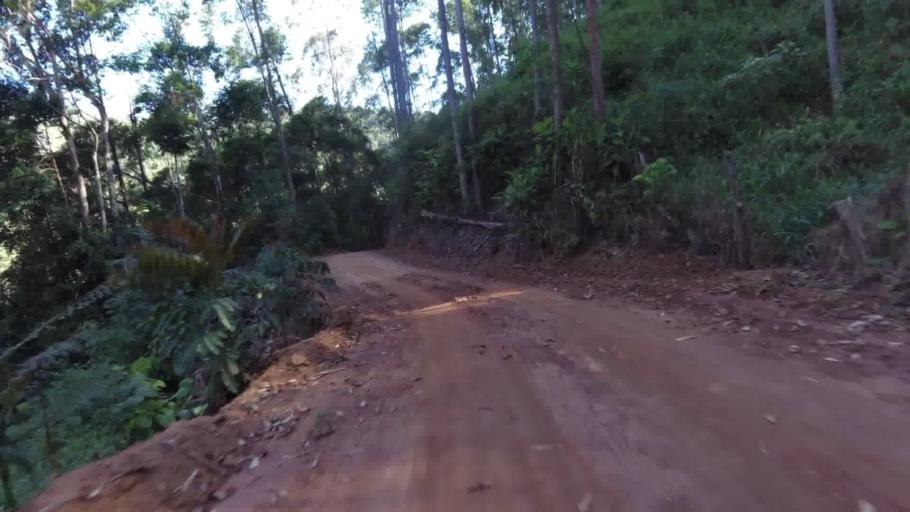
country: BR
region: Espirito Santo
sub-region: Alfredo Chaves
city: Alfredo Chaves
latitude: -20.6051
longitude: -40.7519
